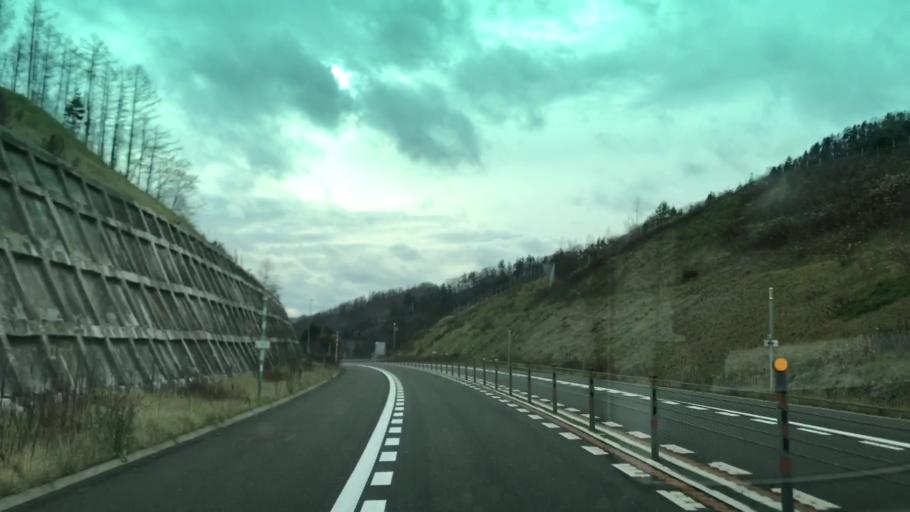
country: JP
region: Hokkaido
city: Iwamizawa
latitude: 42.9310
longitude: 142.0392
